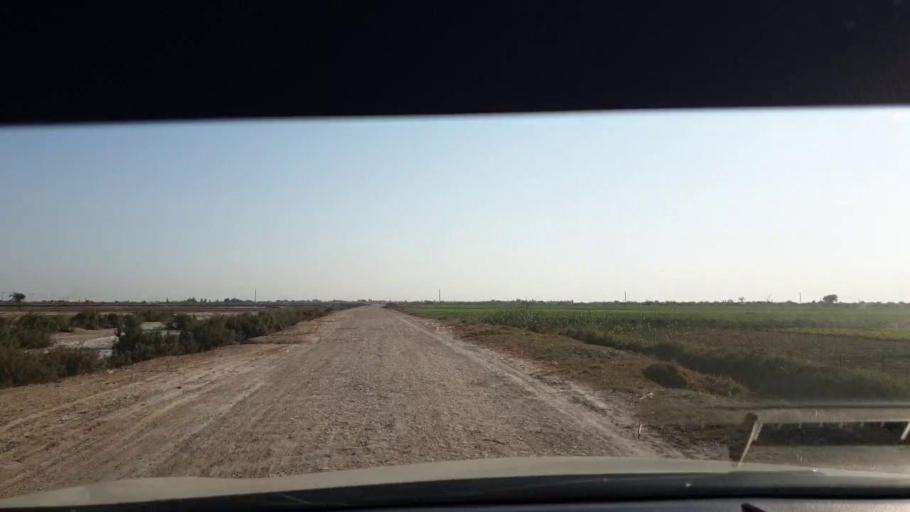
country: PK
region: Sindh
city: Berani
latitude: 25.7932
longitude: 68.9264
